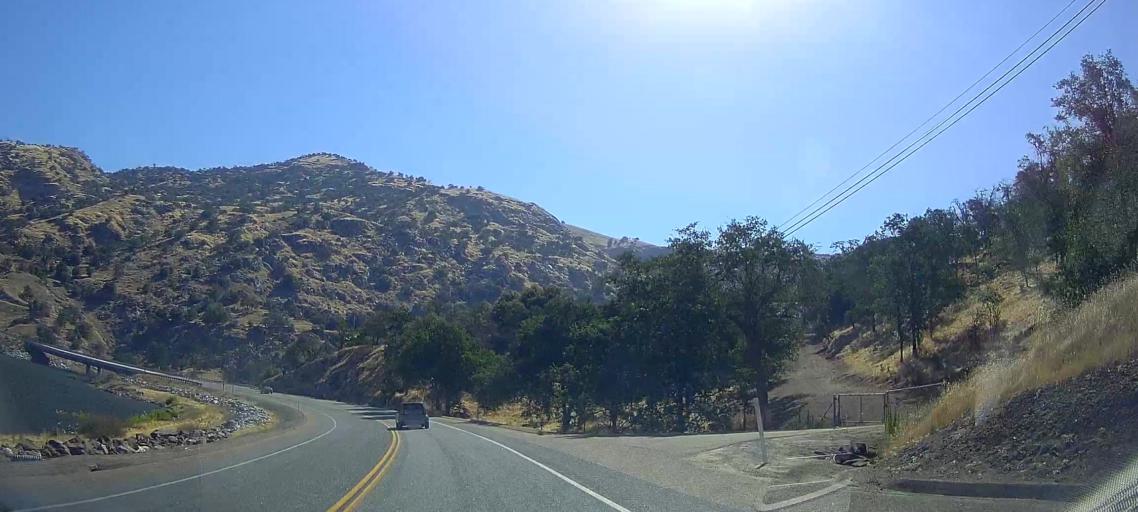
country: US
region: California
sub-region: Tulare County
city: Three Rivers
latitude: 36.3870
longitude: -118.9480
